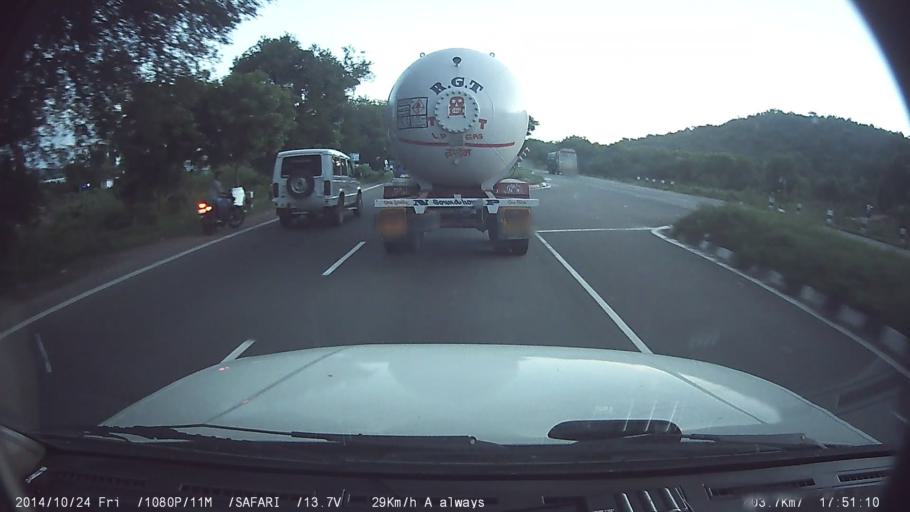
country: IN
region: Tamil Nadu
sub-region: Kancheepuram
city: Chengalpattu
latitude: 12.7195
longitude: 79.9811
